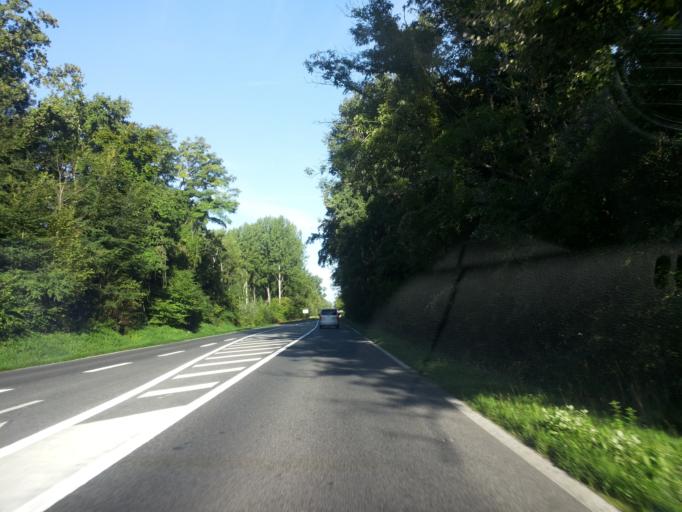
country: FR
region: Picardie
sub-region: Departement de l'Aisne
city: Athies-sous-Laon
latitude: 49.5371
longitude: 3.7477
